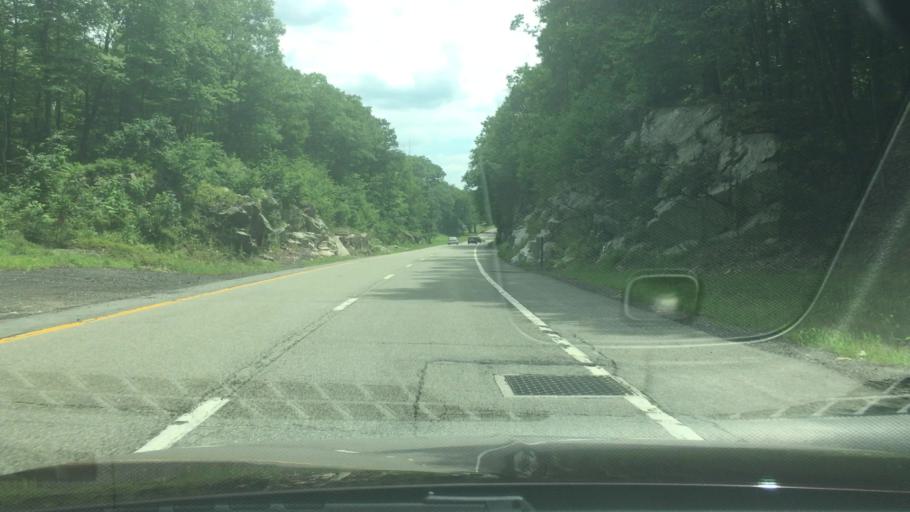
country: US
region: New York
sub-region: Dutchess County
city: Brinckerhoff
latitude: 41.4489
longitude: -73.8164
